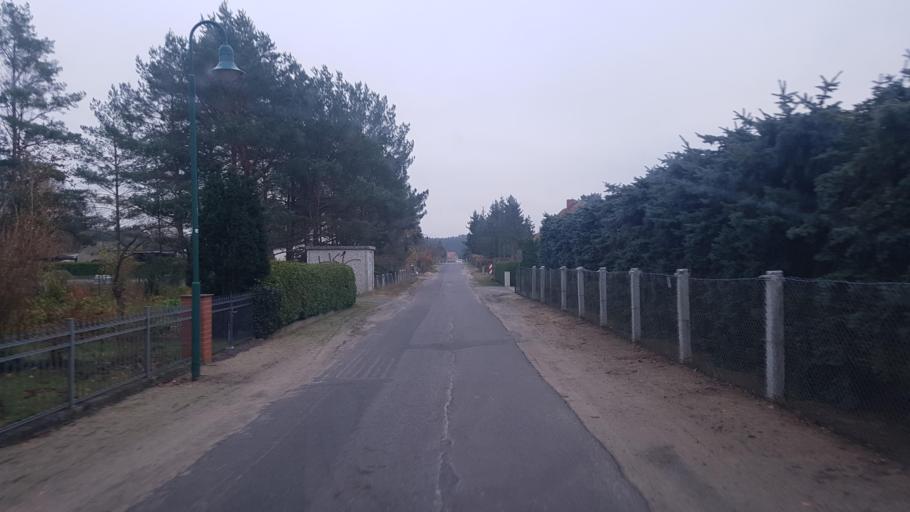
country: DE
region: Brandenburg
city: Gross Kreutz
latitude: 52.3531
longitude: 12.7534
